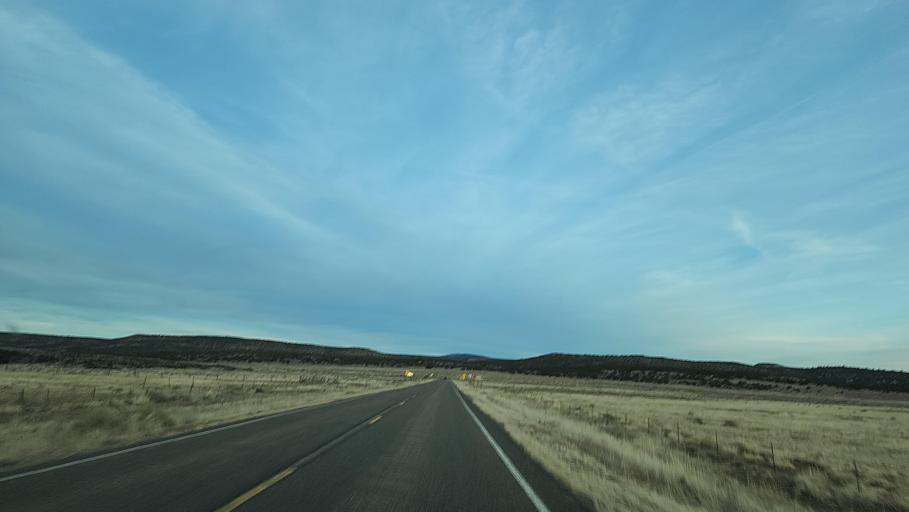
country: US
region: New Mexico
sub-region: Cibola County
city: Grants
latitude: 34.7099
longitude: -107.9953
